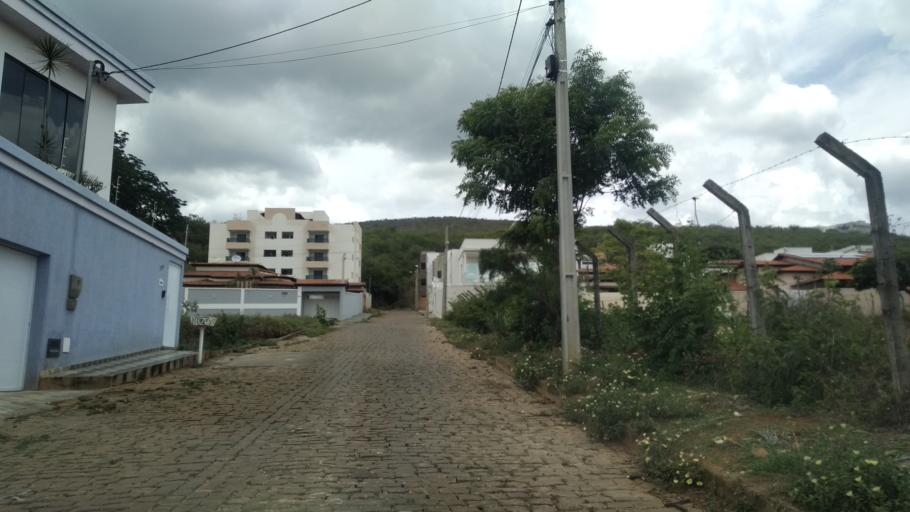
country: BR
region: Bahia
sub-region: Caetite
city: Caetite
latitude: -14.0723
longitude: -42.4797
